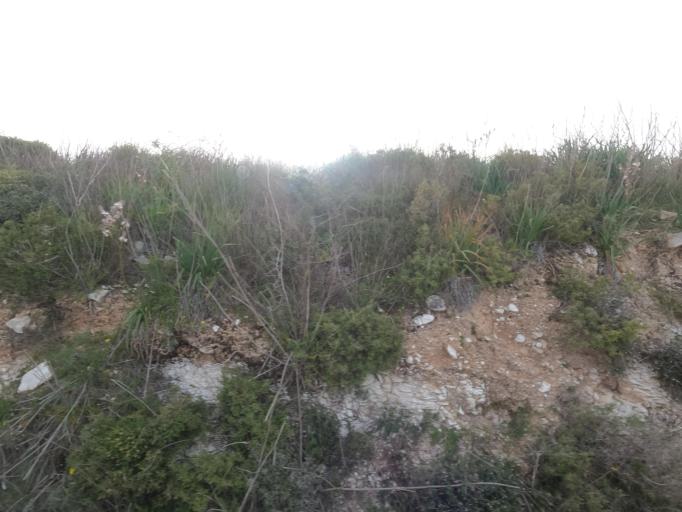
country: CY
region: Pafos
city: Pegeia
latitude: 34.9461
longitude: 32.3750
